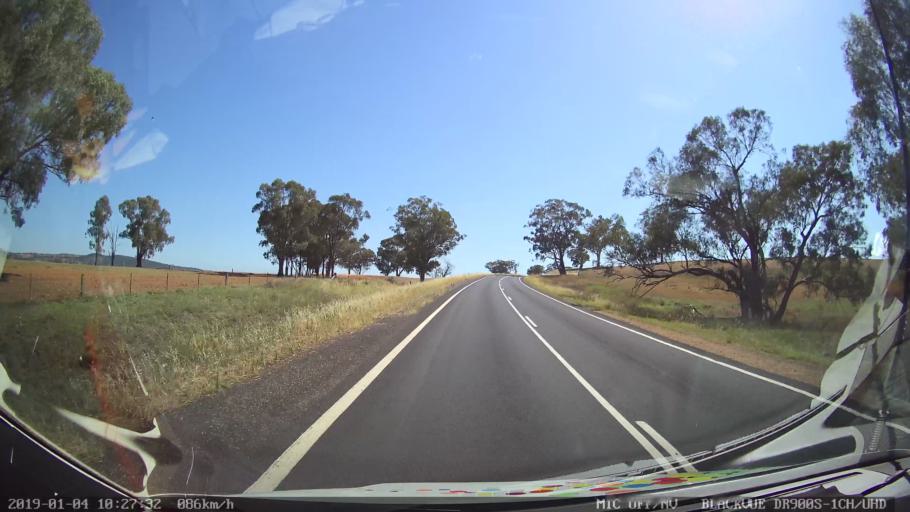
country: AU
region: New South Wales
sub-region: Cabonne
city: Canowindra
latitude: -33.3692
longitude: 148.5991
